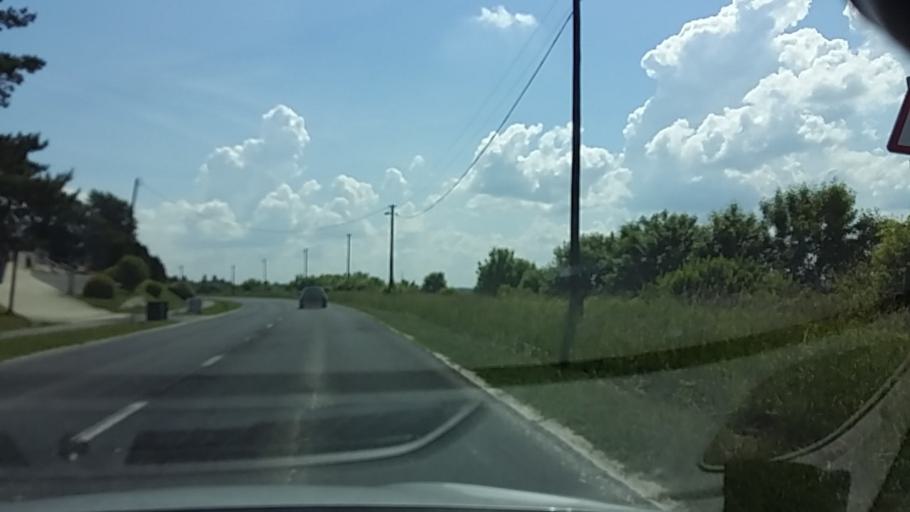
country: AT
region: Burgenland
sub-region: Politischer Bezirk Gussing
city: Inzenhof
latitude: 46.9773
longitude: 16.3548
